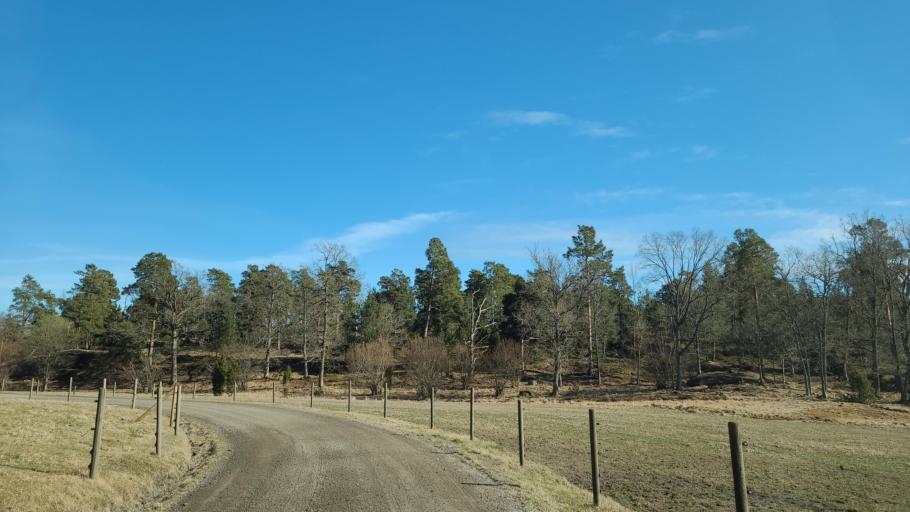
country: SE
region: Stockholm
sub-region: Varmdo Kommun
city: Holo
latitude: 59.2800
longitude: 18.6118
